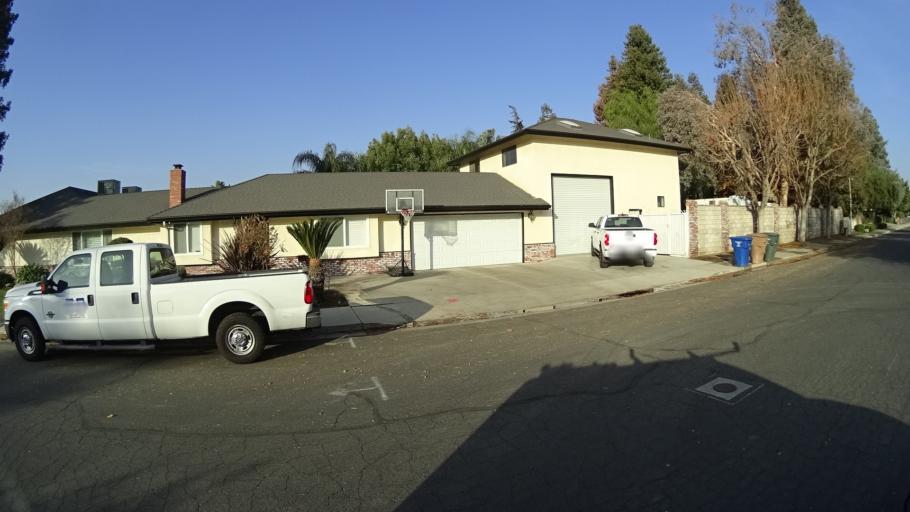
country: US
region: California
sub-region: Kern County
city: Rosedale
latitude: 35.3751
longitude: -119.1330
